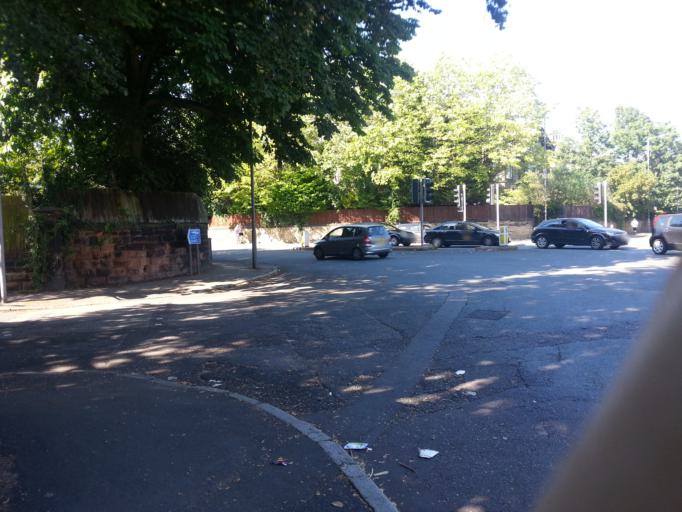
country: GB
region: England
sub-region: Liverpool
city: Liverpool
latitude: 53.3870
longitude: -2.9483
